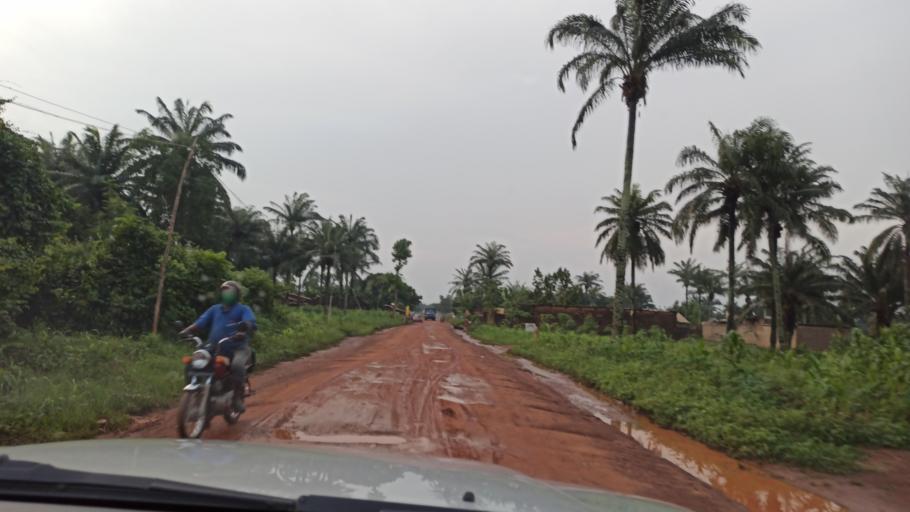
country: BJ
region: Queme
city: Porto-Novo
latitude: 6.5445
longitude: 2.6183
